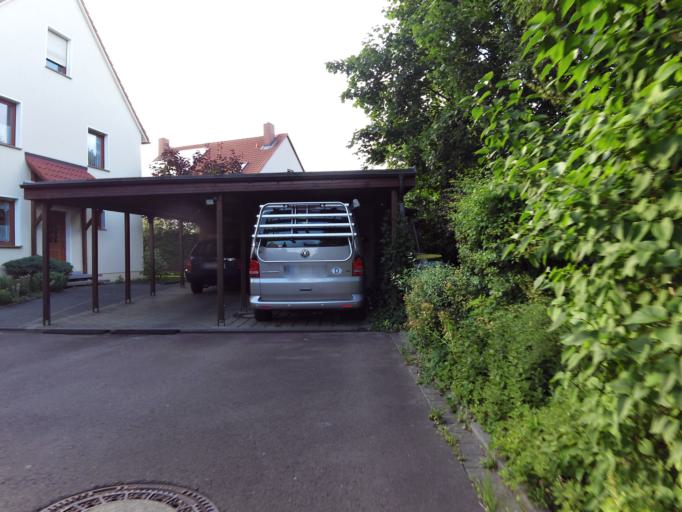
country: DE
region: Saxony
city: Taucha
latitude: 51.3268
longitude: 12.4470
